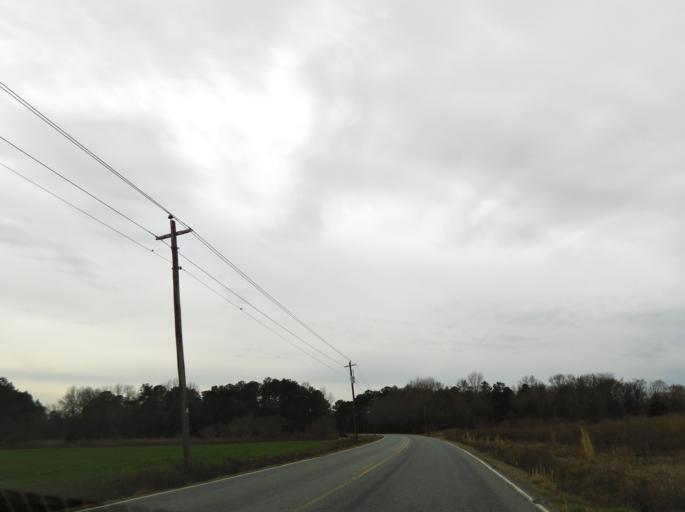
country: US
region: Georgia
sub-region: Houston County
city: Centerville
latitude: 32.7096
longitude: -83.6966
